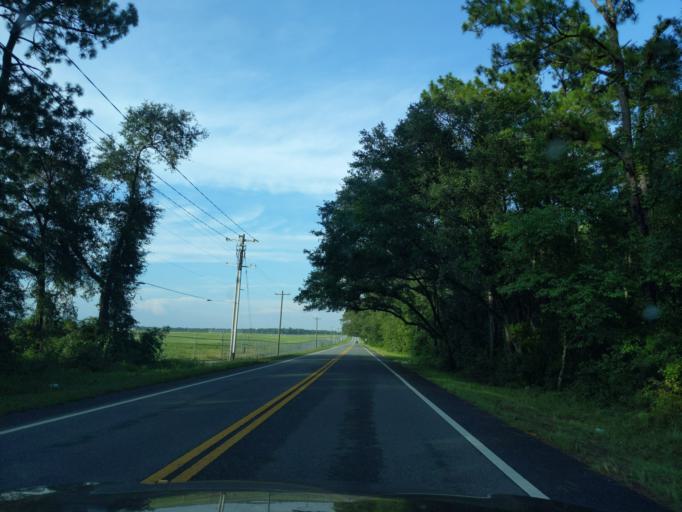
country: US
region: Florida
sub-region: Leon County
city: Tallahassee
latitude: 30.3870
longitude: -84.3310
